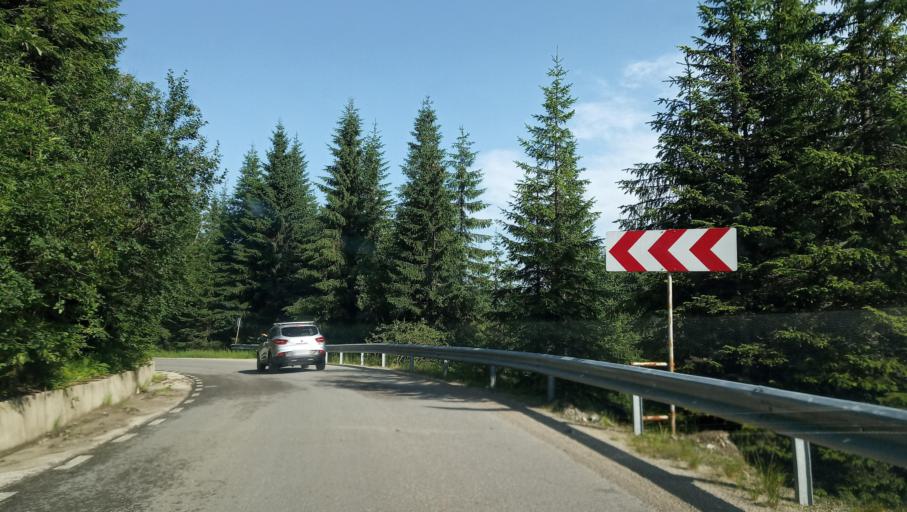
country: RO
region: Dambovita
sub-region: Comuna Moroeni
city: Glod
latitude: 45.3245
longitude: 25.4503
